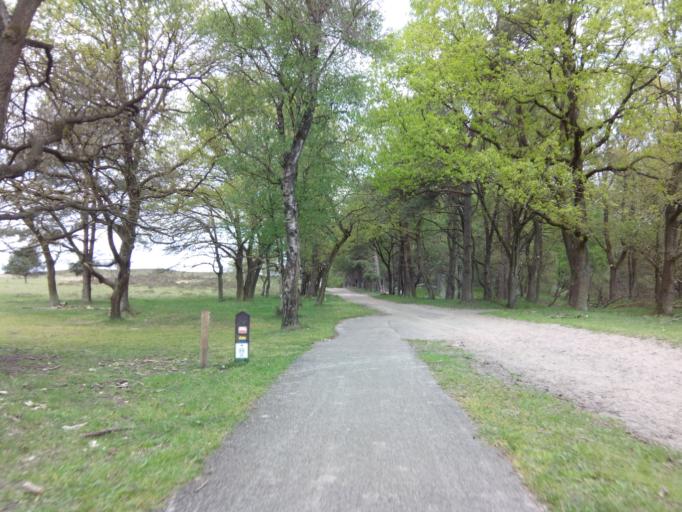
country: NL
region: Gelderland
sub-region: Gemeente Ede
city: Otterlo
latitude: 52.0686
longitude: 5.7576
